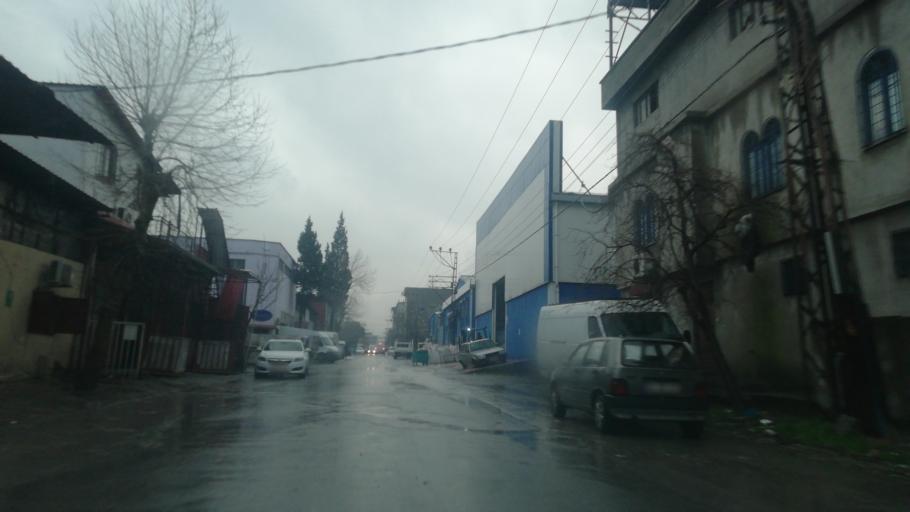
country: TR
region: Kahramanmaras
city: Kahramanmaras
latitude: 37.5590
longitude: 36.9612
